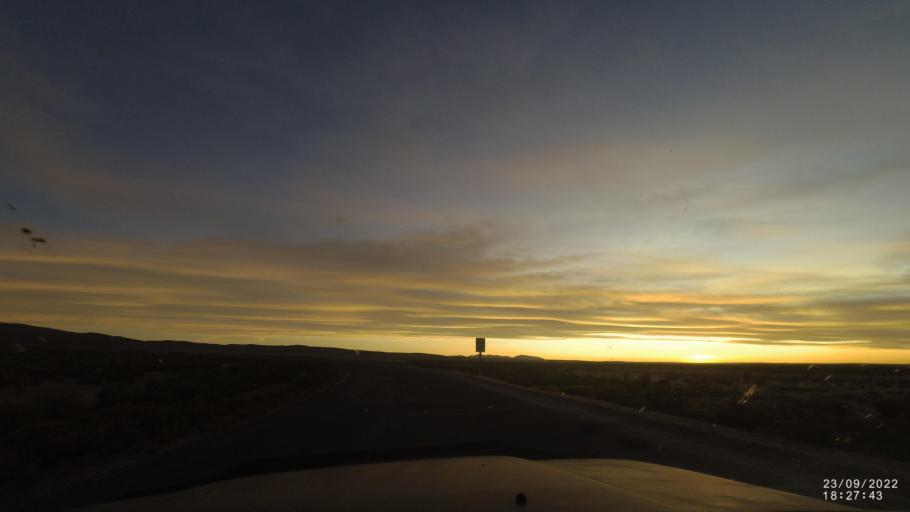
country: BO
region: Oruro
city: Challapata
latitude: -19.3302
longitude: -67.1712
